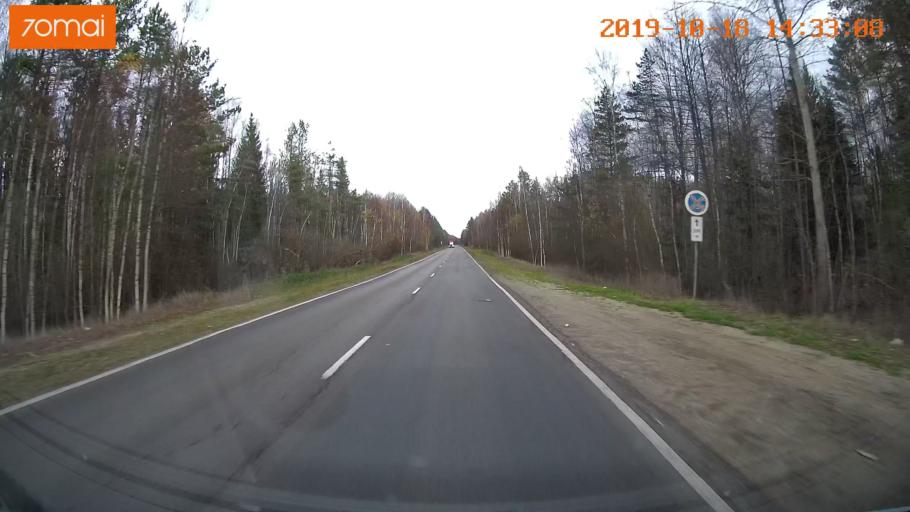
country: RU
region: Rjazan
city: Tuma
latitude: 55.1981
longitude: 40.5912
